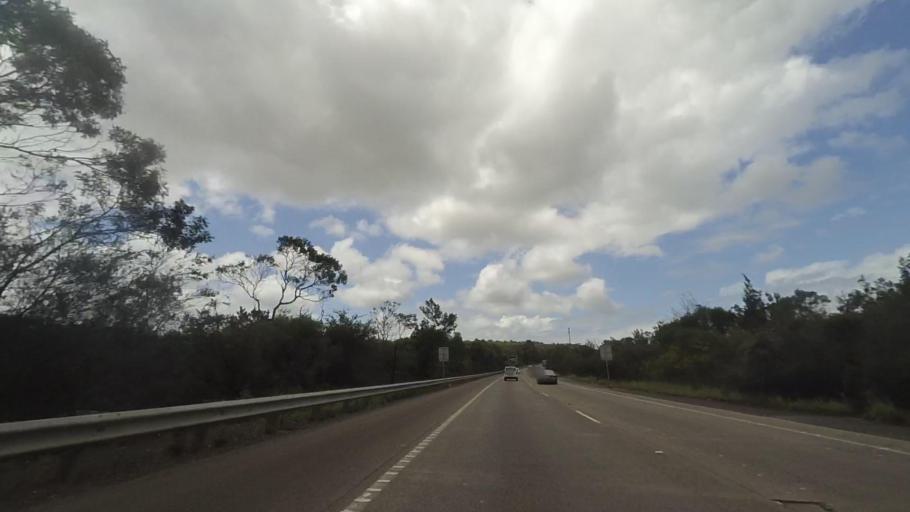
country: AU
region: New South Wales
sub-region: Gosford Shire
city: Narara
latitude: -33.3800
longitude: 151.3001
